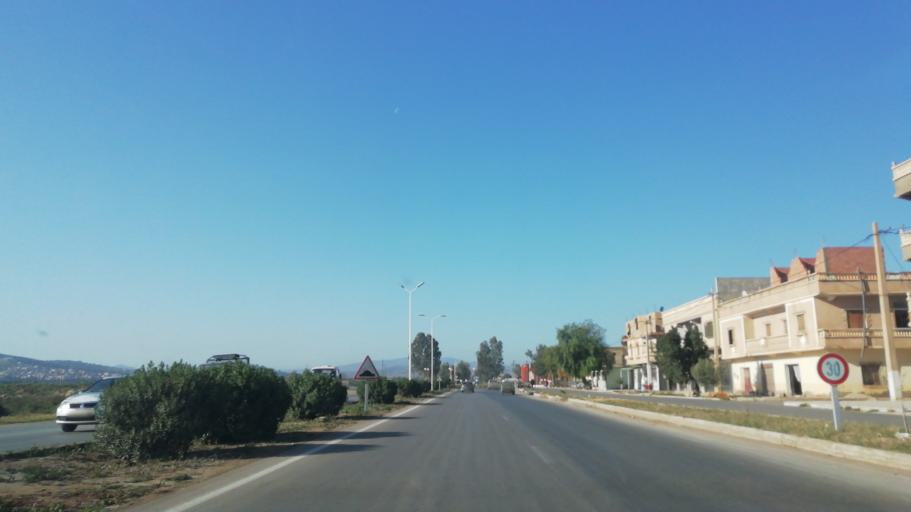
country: DZ
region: Mascara
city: Mascara
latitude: 35.6122
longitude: 0.1006
